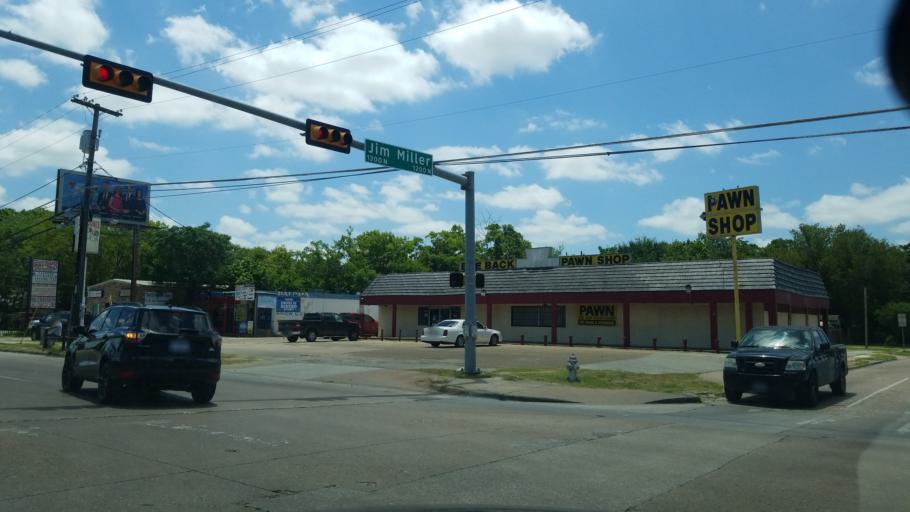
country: US
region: Texas
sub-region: Dallas County
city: Balch Springs
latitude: 32.7343
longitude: -96.7001
